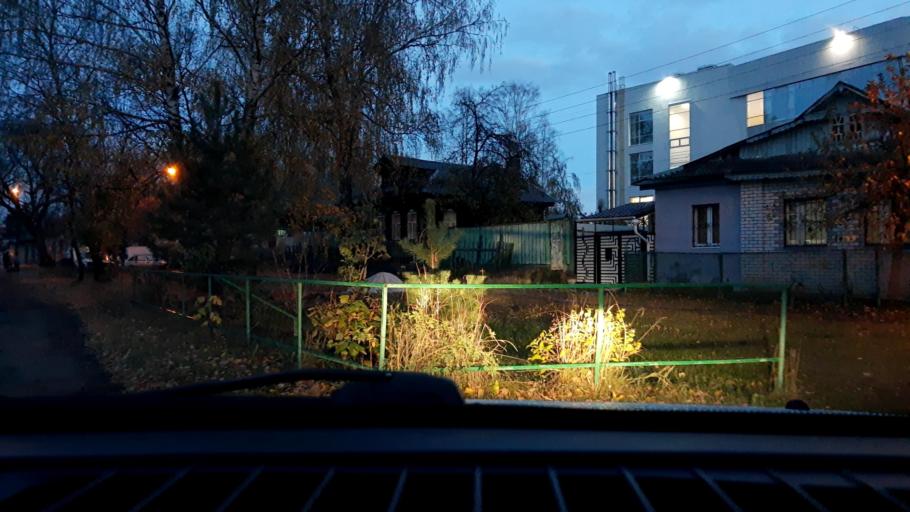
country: RU
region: Nizjnij Novgorod
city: Neklyudovo
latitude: 56.3544
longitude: 43.8500
